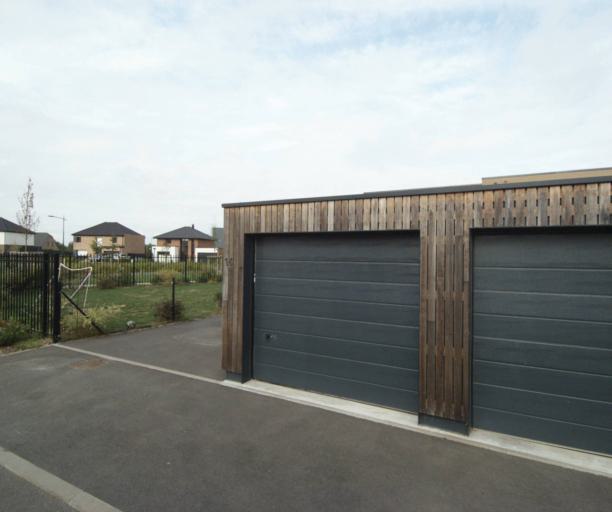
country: FR
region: Nord-Pas-de-Calais
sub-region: Departement du Nord
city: Ronchin
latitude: 50.5845
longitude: 3.0992
